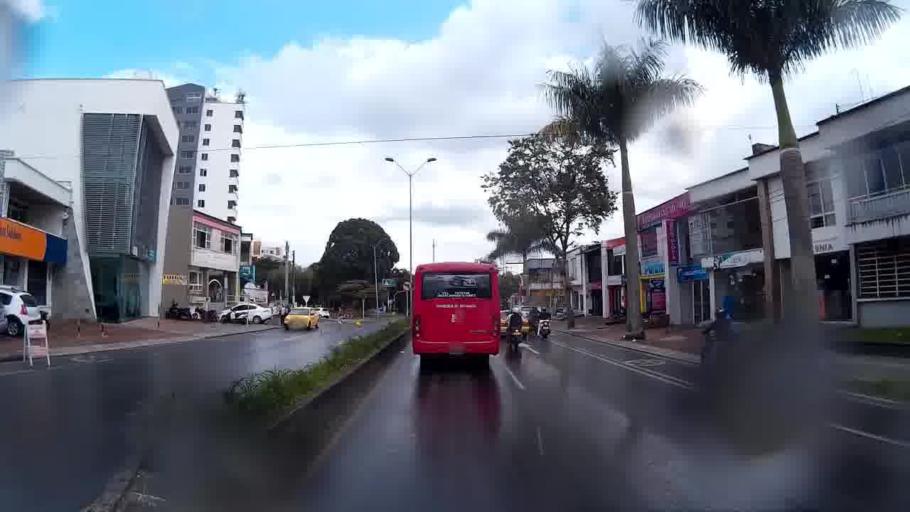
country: CO
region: Quindio
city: Armenia
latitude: 4.5476
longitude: -75.6616
